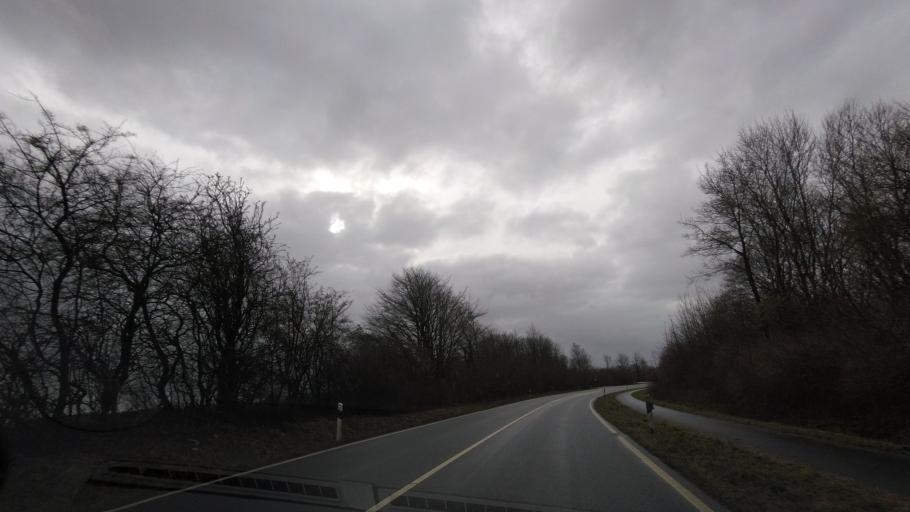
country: DE
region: Schleswig-Holstein
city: Schaalby
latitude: 54.5576
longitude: 9.6268
